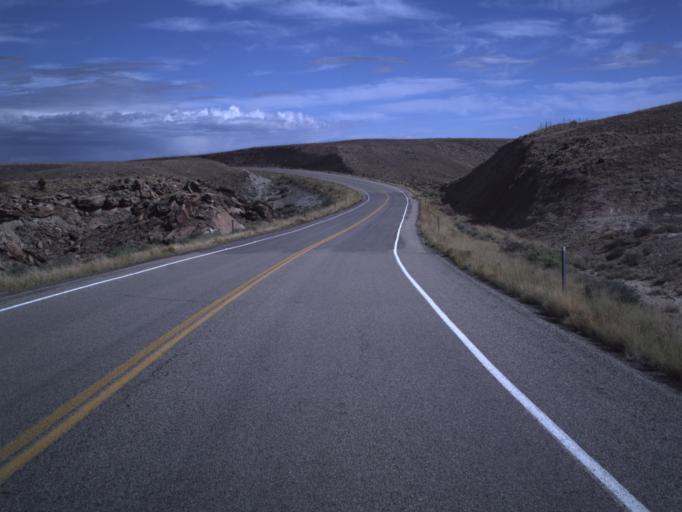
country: US
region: Colorado
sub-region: Montezuma County
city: Towaoc
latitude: 37.1740
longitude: -109.1006
